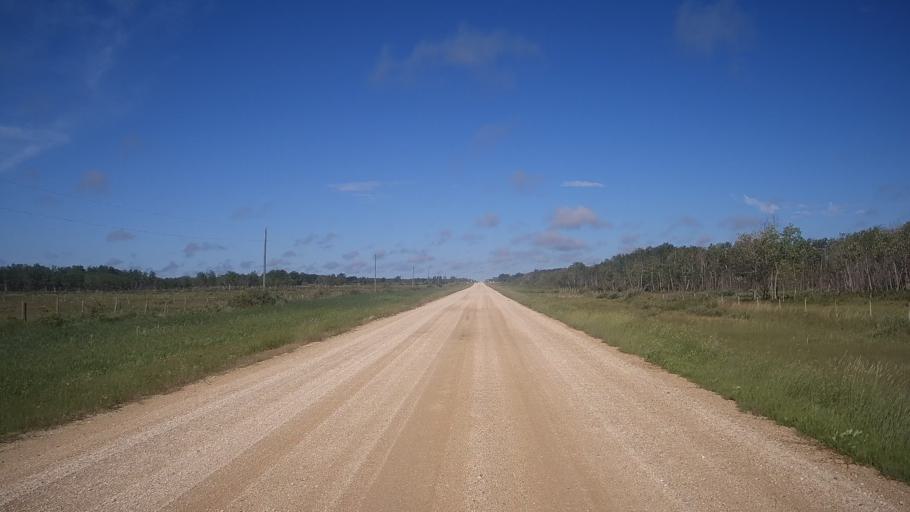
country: CA
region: Manitoba
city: Stonewall
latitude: 50.2411
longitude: -97.7235
